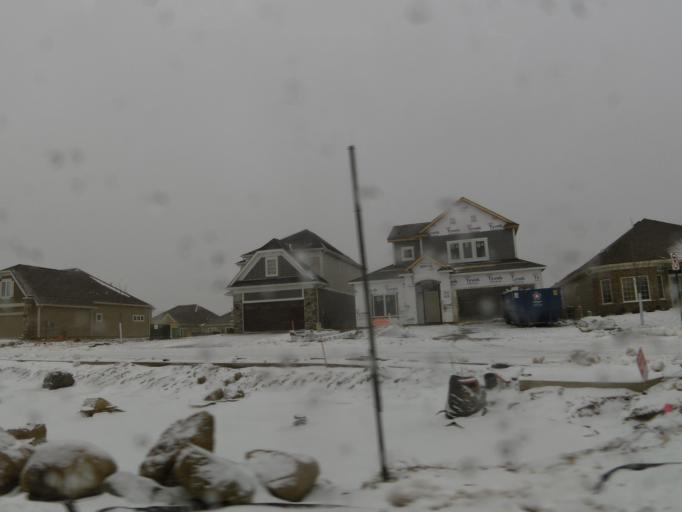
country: US
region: Minnesota
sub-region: Washington County
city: Oakdale
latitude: 44.9627
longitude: -92.9260
